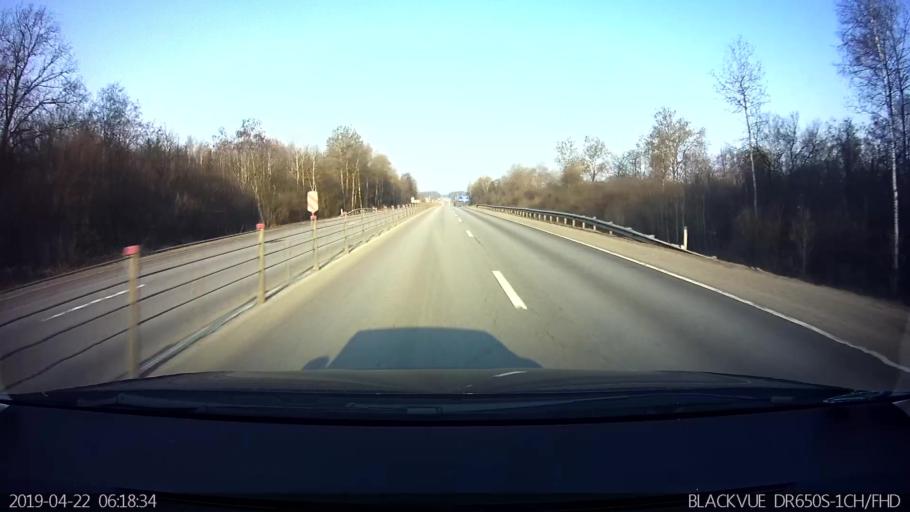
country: RU
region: Moskovskaya
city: Mozhaysk
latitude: 55.4634
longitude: 35.9548
